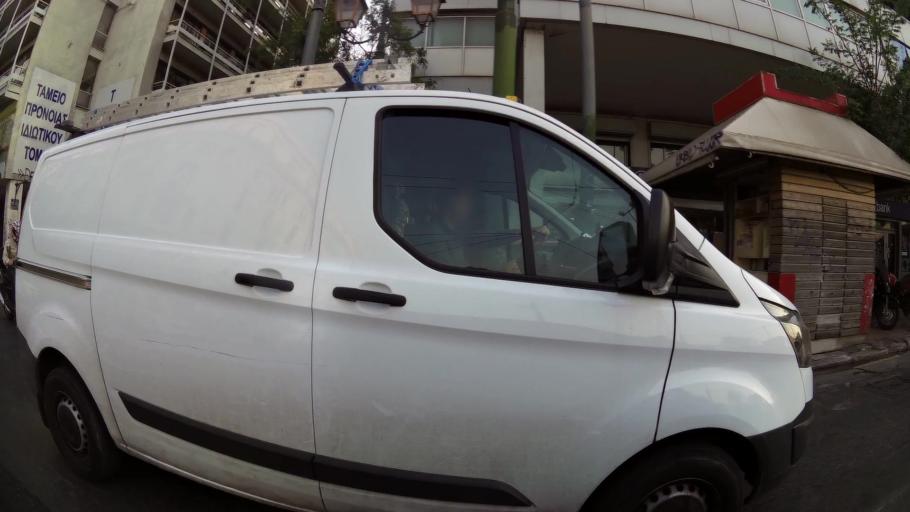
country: GR
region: Attica
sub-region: Nomarchia Athinas
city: Athens
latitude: 37.9819
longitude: 23.7340
